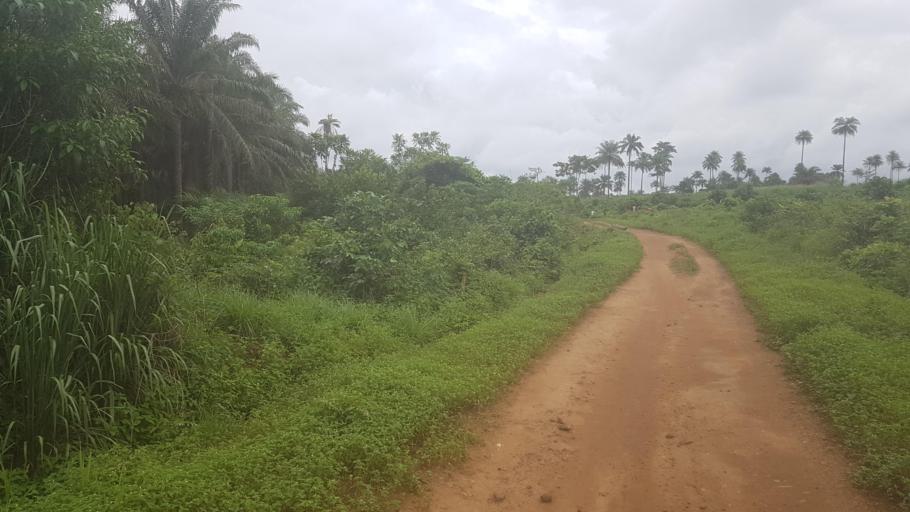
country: SL
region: Southern Province
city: Sumbuya
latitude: 7.5453
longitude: -12.1682
